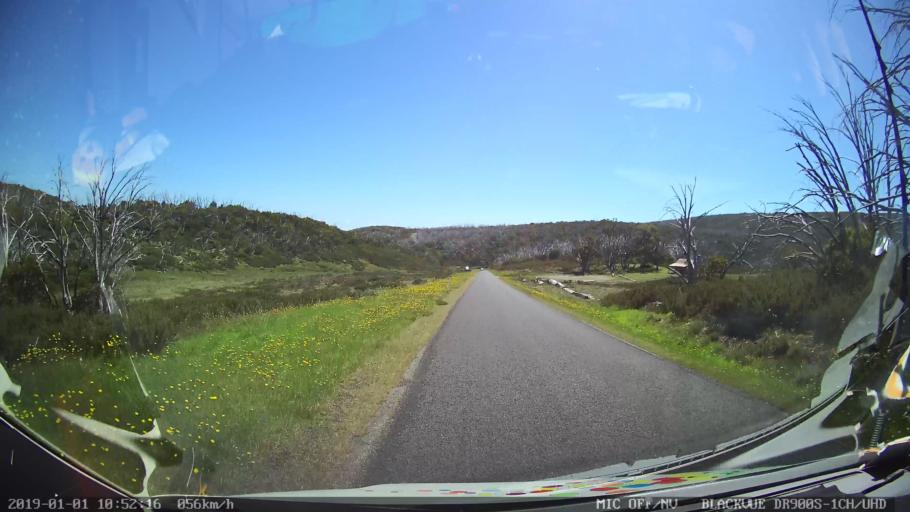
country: AU
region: New South Wales
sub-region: Snowy River
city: Jindabyne
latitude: -36.0166
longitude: 148.3783
